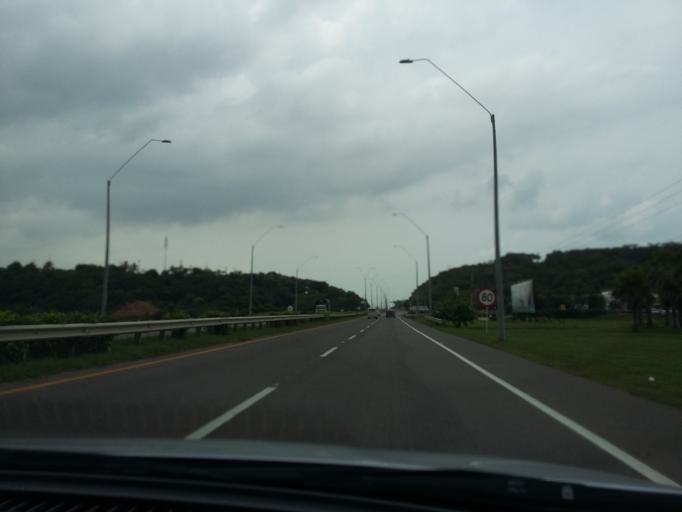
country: CO
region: Bolivar
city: Santa Rosa
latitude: 10.5181
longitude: -75.4680
